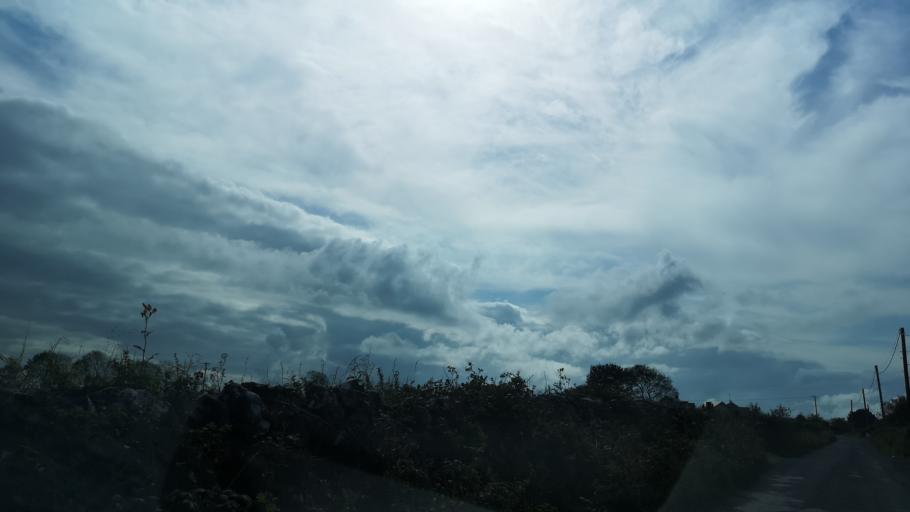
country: IE
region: Connaught
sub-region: County Galway
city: Athenry
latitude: 53.3110
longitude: -8.8072
